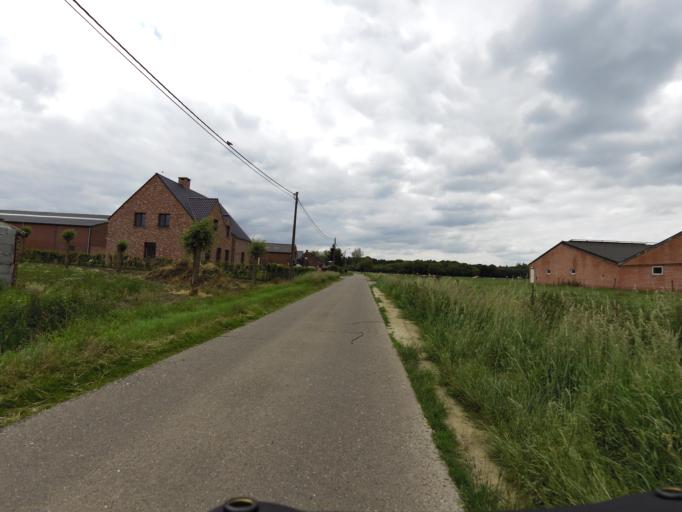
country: BE
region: Flanders
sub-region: Provincie Antwerpen
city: Baarle-Hertog
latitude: 51.4773
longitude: 4.8333
